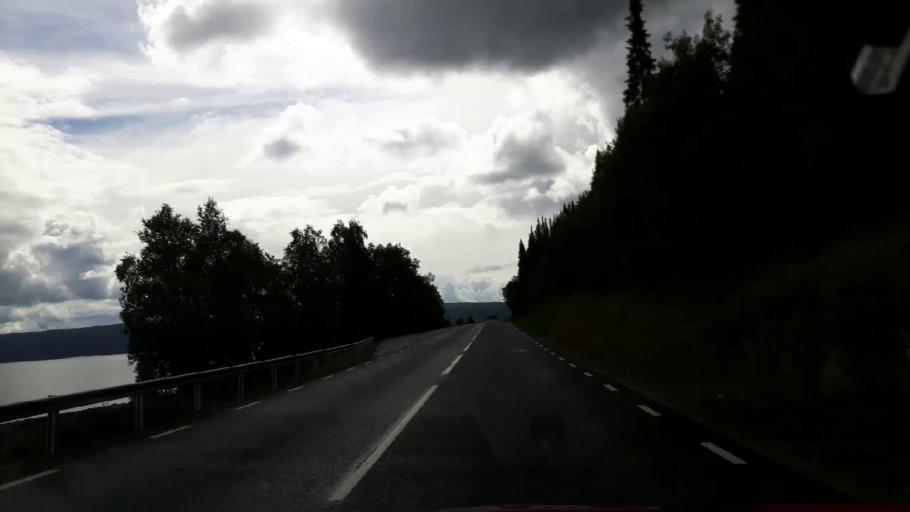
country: NO
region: Nord-Trondelag
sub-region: Royrvik
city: Royrvik
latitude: 64.8294
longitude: 14.0792
